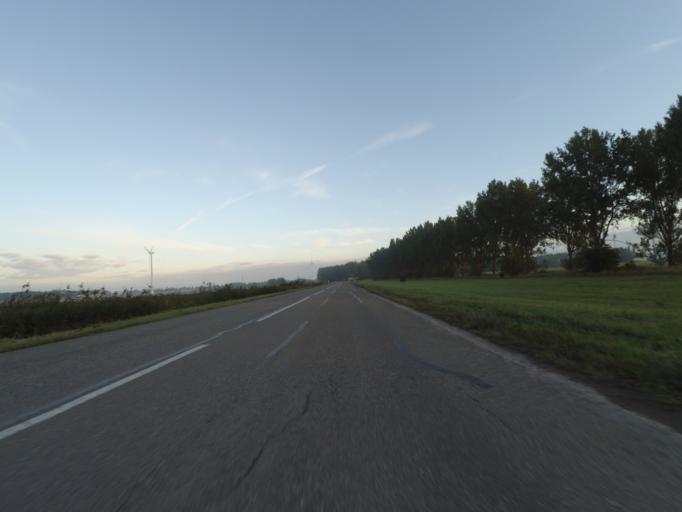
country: NL
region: Utrecht
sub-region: Gemeente Bunschoten
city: Bunschoten
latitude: 52.3231
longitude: 5.4289
